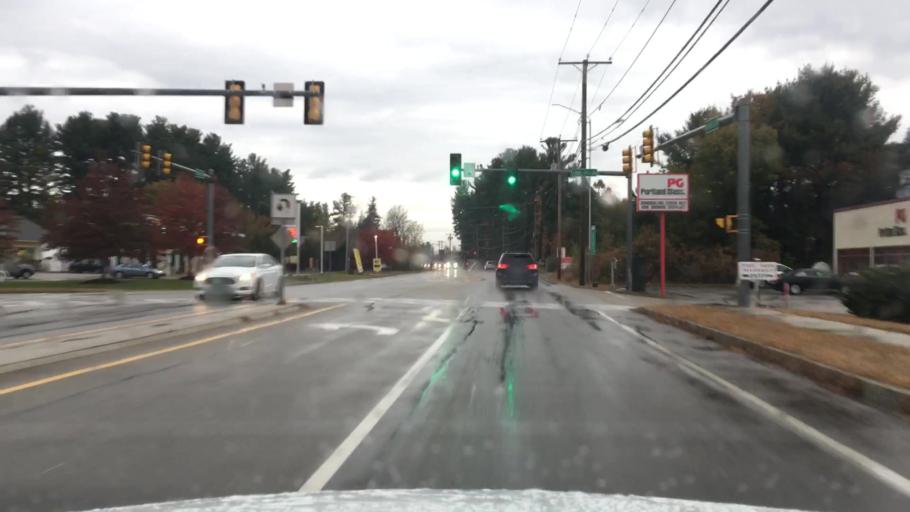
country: US
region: New Hampshire
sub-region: Strafford County
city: Dover
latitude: 43.2316
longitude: -70.8970
